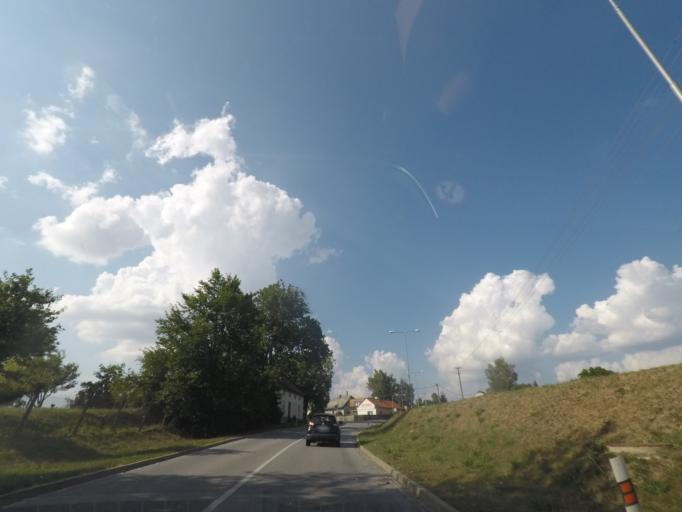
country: CZ
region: Kralovehradecky
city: Dvur Kralove nad Labem
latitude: 50.4564
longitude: 15.8587
